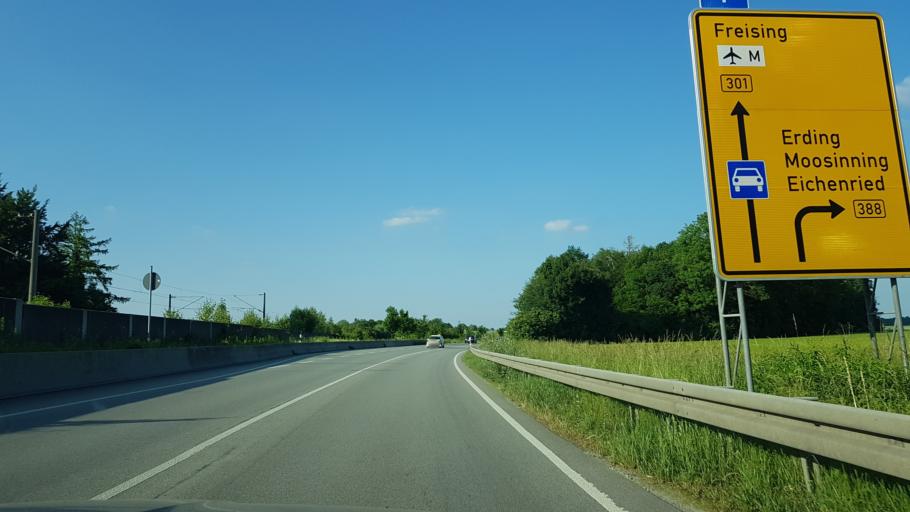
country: DE
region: Bavaria
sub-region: Upper Bavaria
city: Ismaning
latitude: 48.2517
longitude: 11.7025
